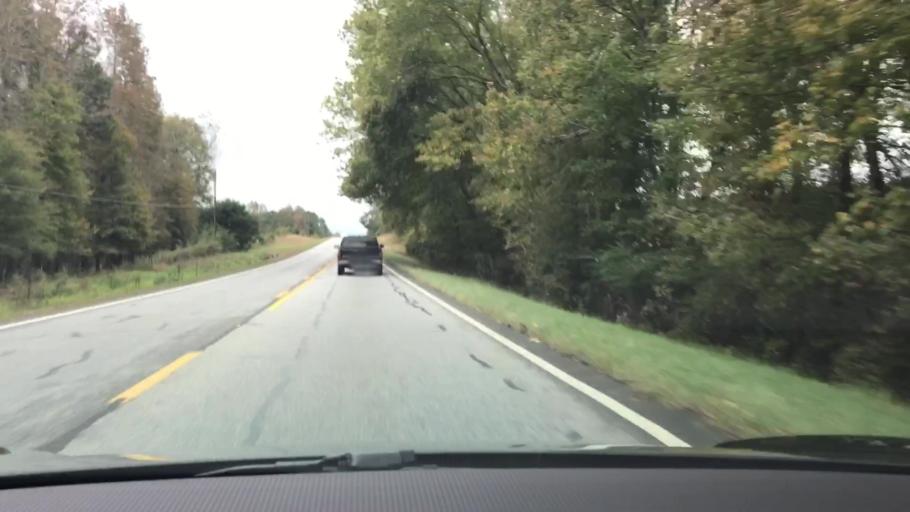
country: US
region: Georgia
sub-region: Oconee County
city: Watkinsville
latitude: 33.8496
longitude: -83.3949
